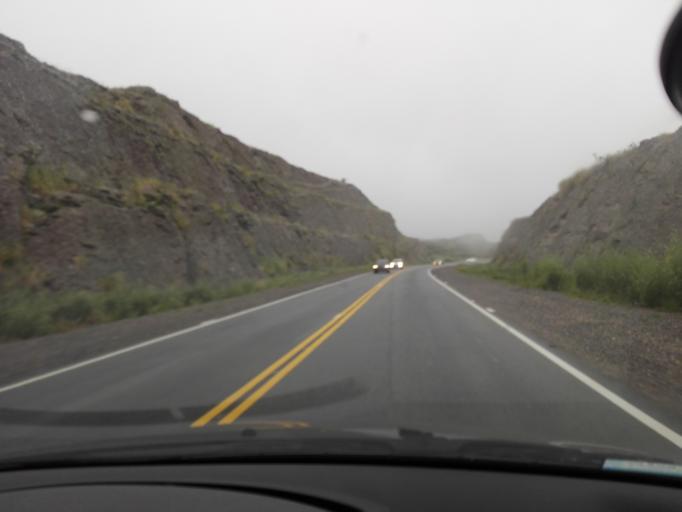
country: AR
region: Cordoba
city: Cuesta Blanca
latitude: -31.5986
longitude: -64.7098
